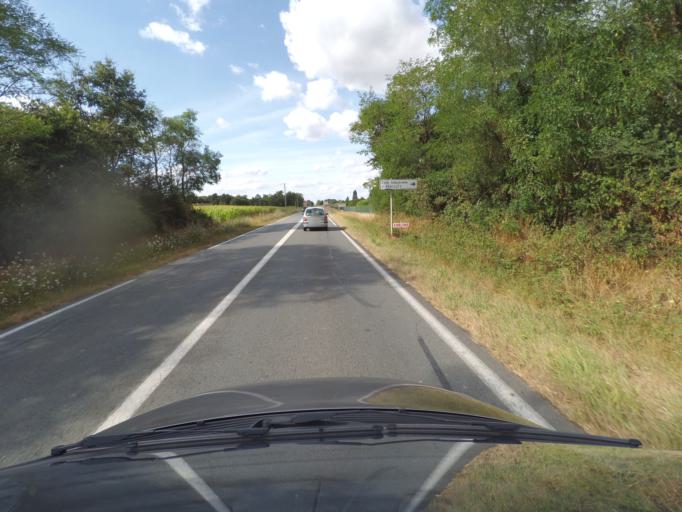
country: FR
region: Poitou-Charentes
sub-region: Departement de la Vienne
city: Cenon-sur-Vienne
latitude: 46.7571
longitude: 0.5537
